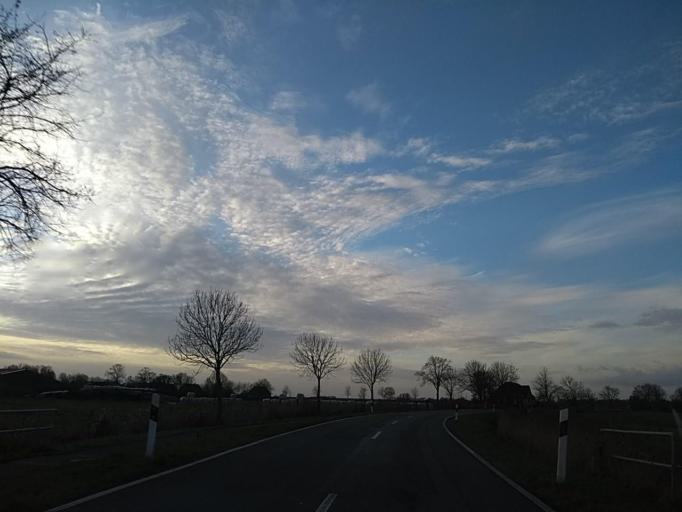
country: DE
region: Lower Saxony
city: Jemgum
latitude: 53.3104
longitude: 7.2989
